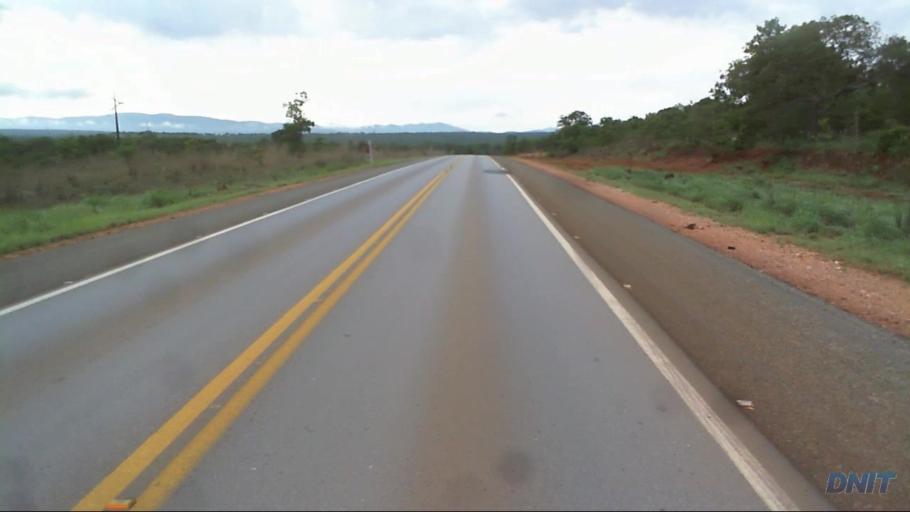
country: BR
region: Goias
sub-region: Uruacu
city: Uruacu
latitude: -14.7397
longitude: -49.0832
